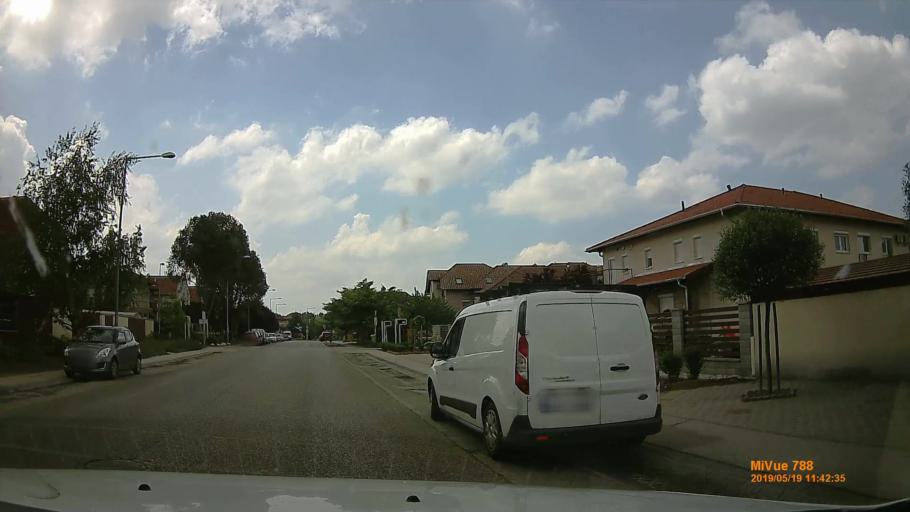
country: HU
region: Budapest
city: Budapest XVII. keruelet
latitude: 47.4702
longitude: 19.2277
